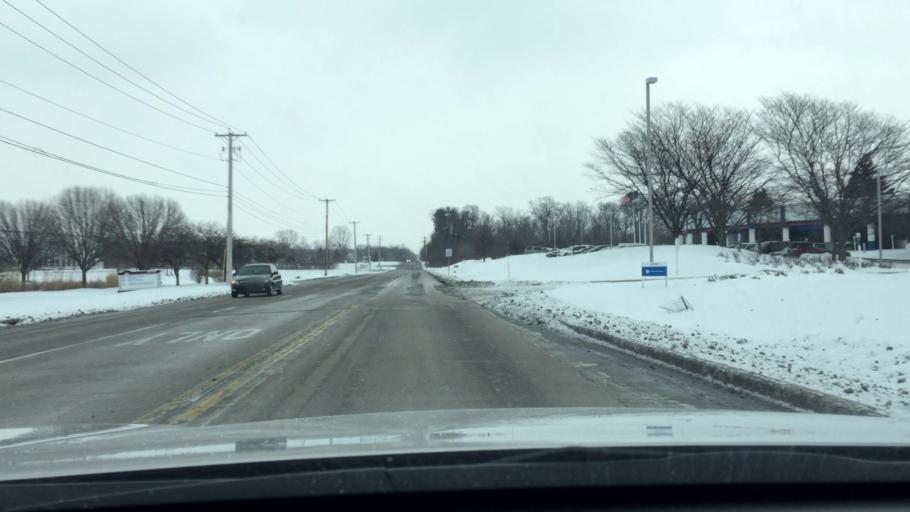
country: US
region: Indiana
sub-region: Hamilton County
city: Fishers
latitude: 39.9643
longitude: -85.9934
